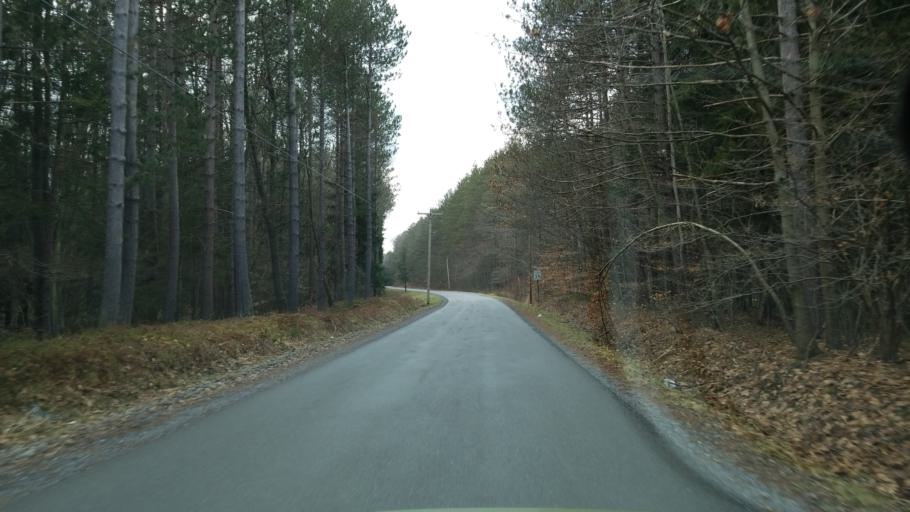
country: US
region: Pennsylvania
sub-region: Clearfield County
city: Treasure Lake
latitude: 41.1472
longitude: -78.5553
